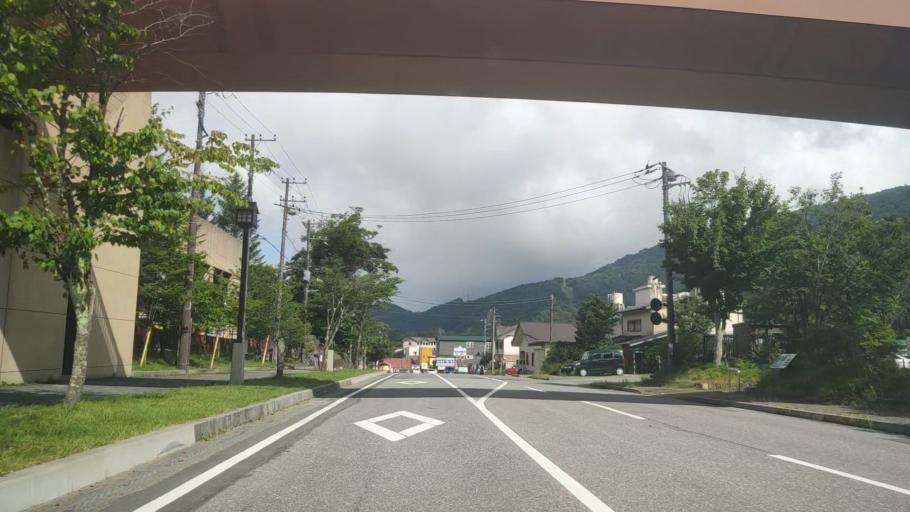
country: JP
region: Tochigi
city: Nikko
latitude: 36.7407
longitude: 139.4928
